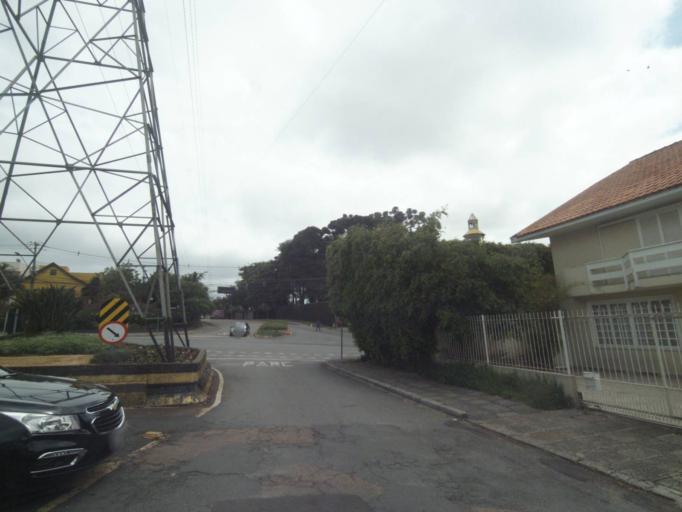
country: BR
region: Parana
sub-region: Curitiba
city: Curitiba
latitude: -25.3858
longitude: -49.2797
